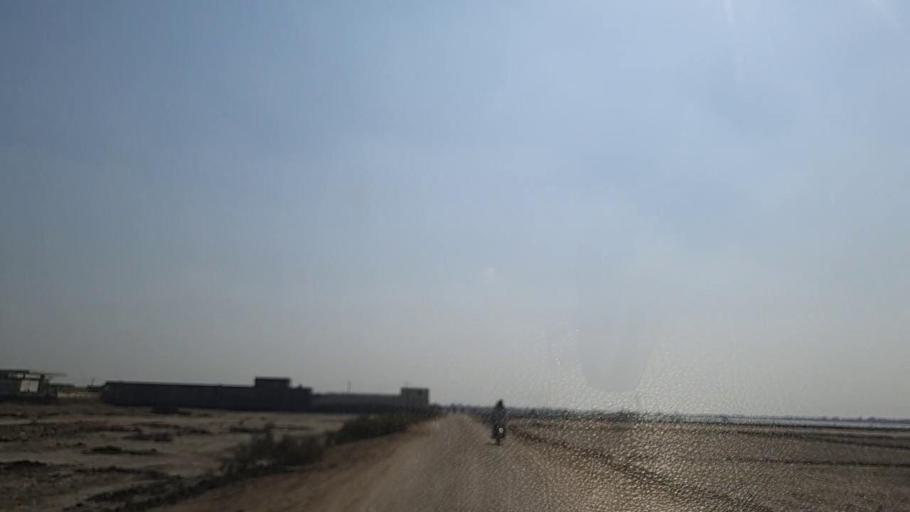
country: PK
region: Sindh
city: Daur
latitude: 26.4646
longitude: 68.2504
